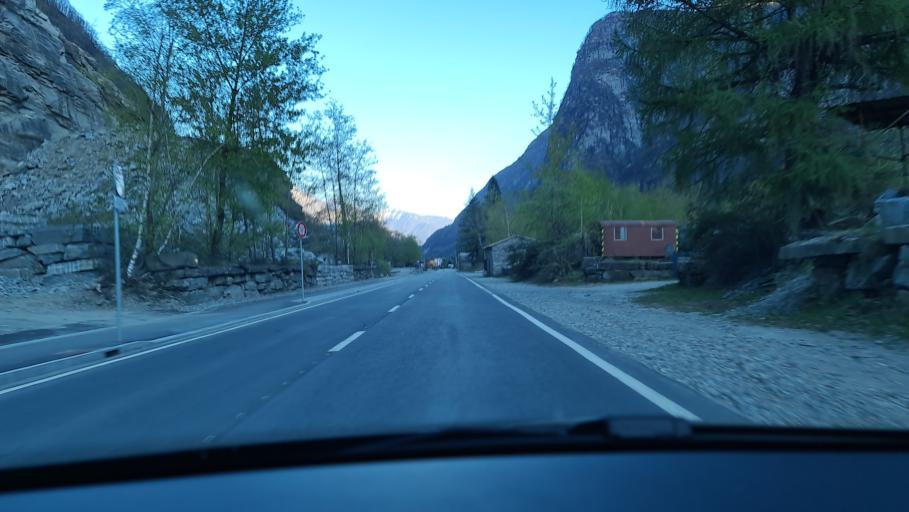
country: CH
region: Ticino
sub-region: Vallemaggia District
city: Cevio
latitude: 46.3010
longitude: 8.6214
